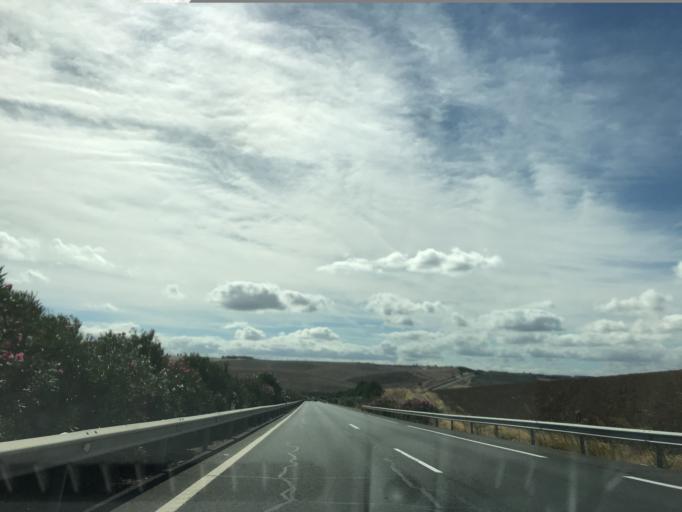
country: ES
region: Andalusia
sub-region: Province of Cordoba
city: La Victoria
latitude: 37.7422
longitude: -4.8497
